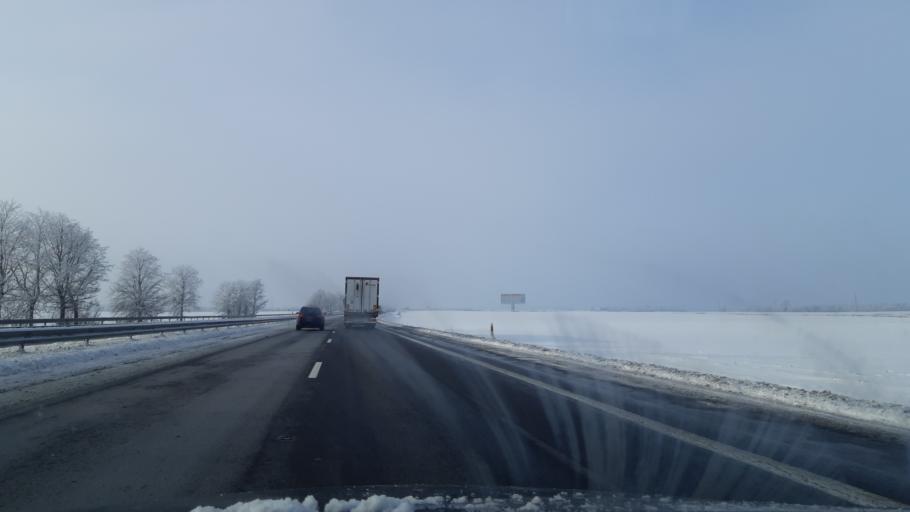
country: LT
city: Kaisiadorys
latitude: 54.8595
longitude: 24.2745
